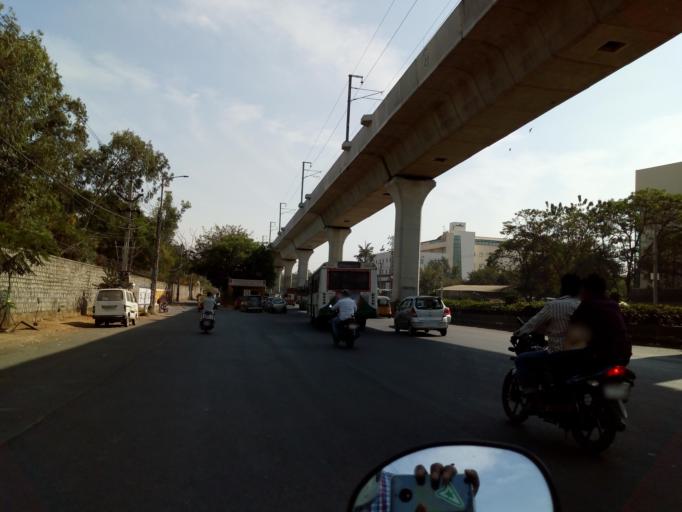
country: IN
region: Telangana
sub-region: Rangareddi
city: Uppal Kalan
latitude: 17.4125
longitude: 78.5490
